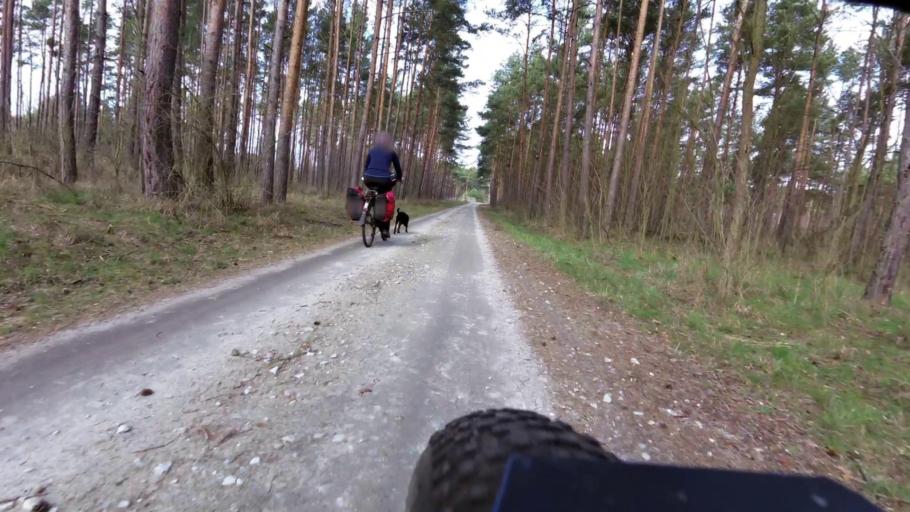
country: DE
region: Brandenburg
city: Wiesenau
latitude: 52.2846
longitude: 14.6437
